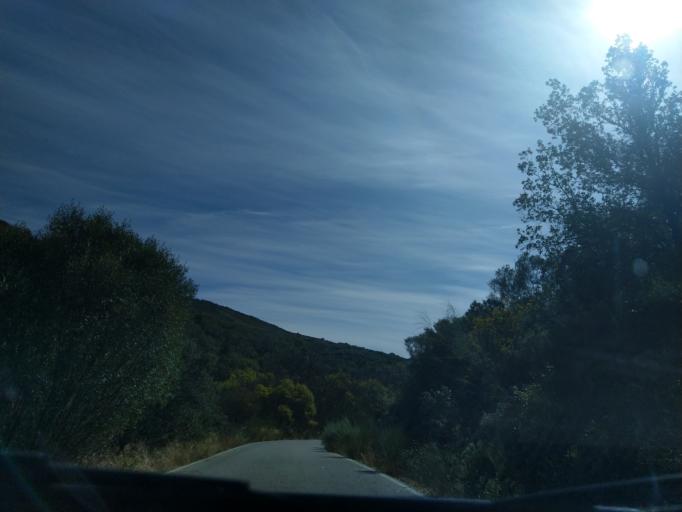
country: ES
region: Extremadura
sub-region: Provincia de Badajoz
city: Reina
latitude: 38.1198
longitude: -5.9146
